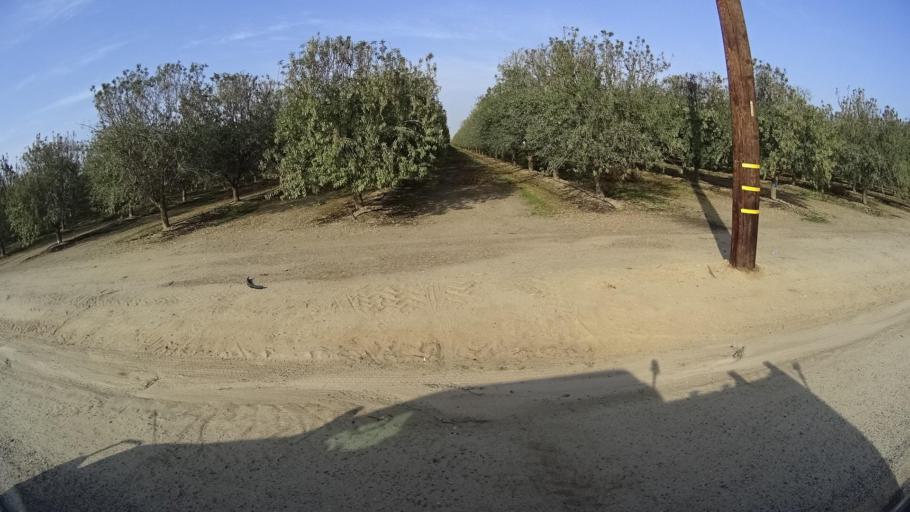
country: US
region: California
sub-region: Tulare County
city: Richgrove
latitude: 35.7761
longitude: -119.1493
